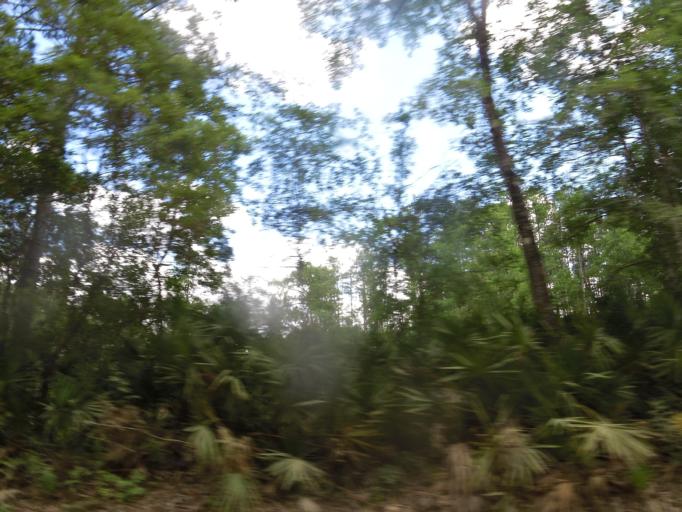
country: US
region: Florida
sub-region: Clay County
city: Asbury Lake
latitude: 29.8925
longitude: -81.8727
